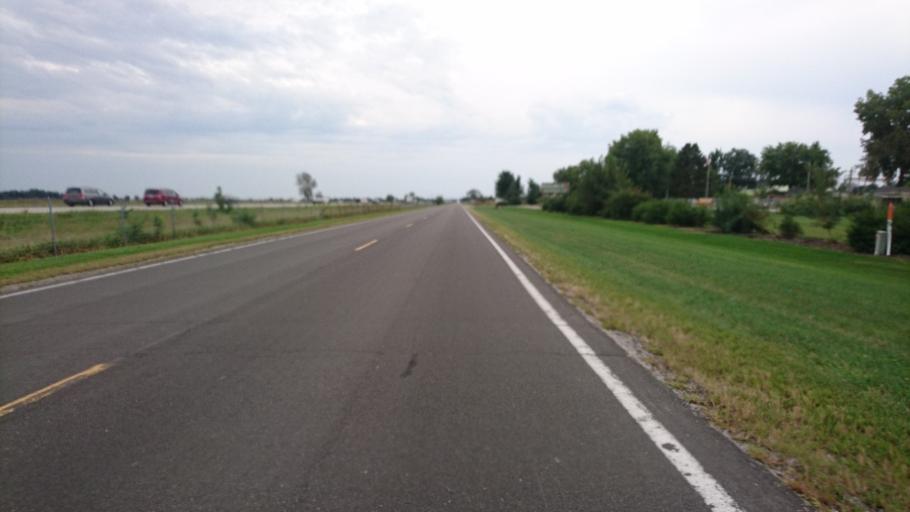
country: US
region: Illinois
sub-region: Sangamon County
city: Chatham
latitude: 39.6586
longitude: -89.6480
